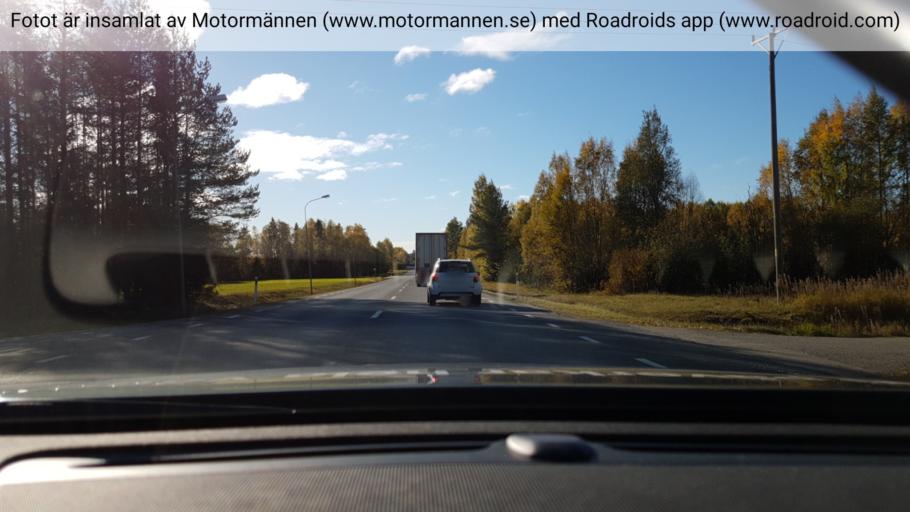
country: SE
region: Vaesterbotten
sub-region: Skelleftea Kommun
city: Burea
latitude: 64.5174
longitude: 21.2583
